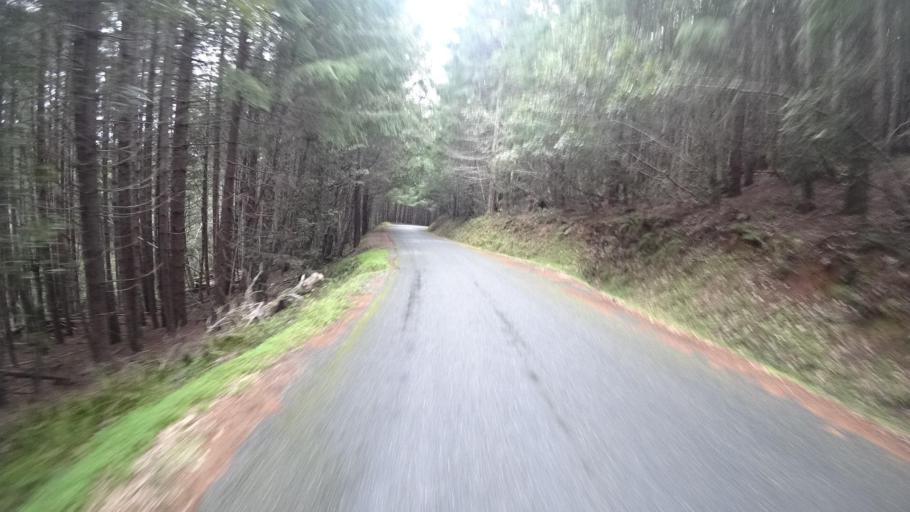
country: US
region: California
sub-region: Humboldt County
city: Willow Creek
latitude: 41.2021
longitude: -123.7807
